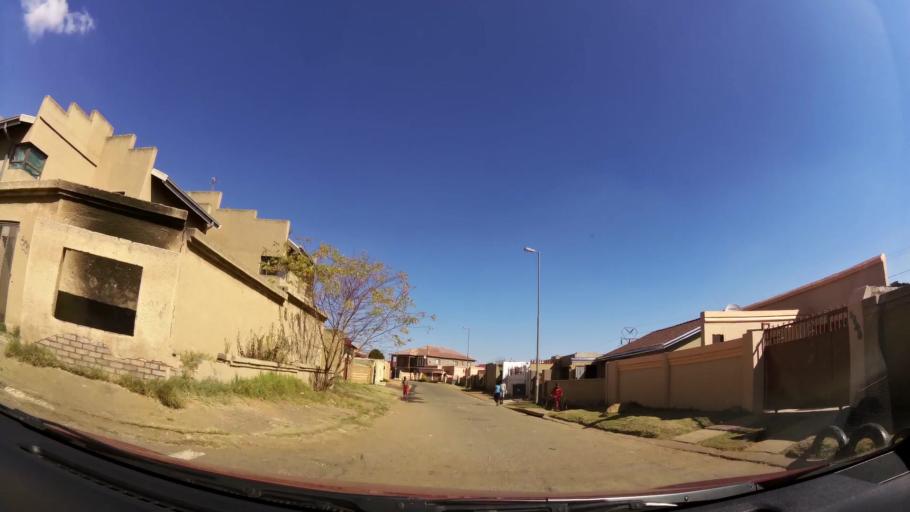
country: ZA
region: Gauteng
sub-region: City of Johannesburg Metropolitan Municipality
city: Soweto
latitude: -26.2388
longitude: 27.8166
